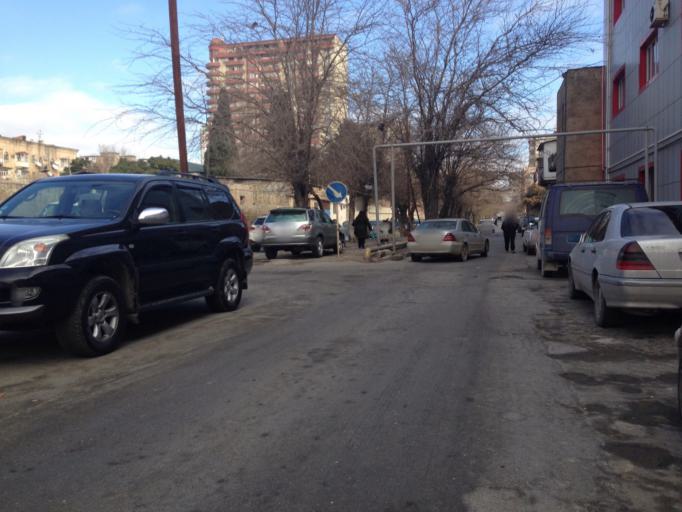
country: AZ
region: Baki
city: Baku
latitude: 40.3913
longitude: 49.8598
